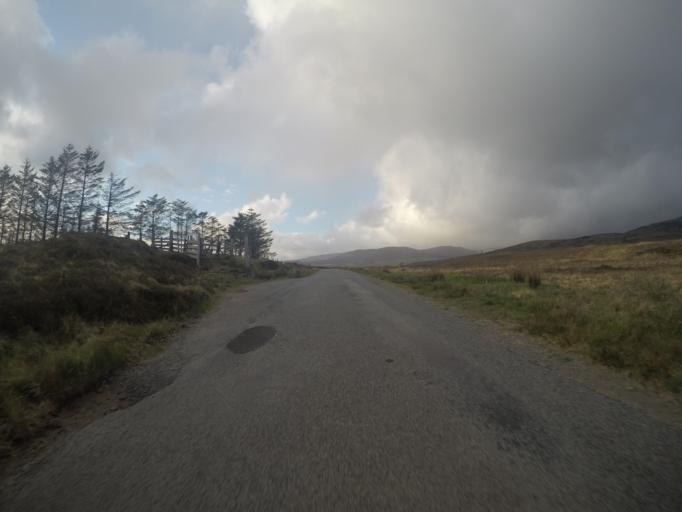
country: GB
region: Scotland
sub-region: Highland
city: Isle of Skye
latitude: 57.4582
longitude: -6.2970
